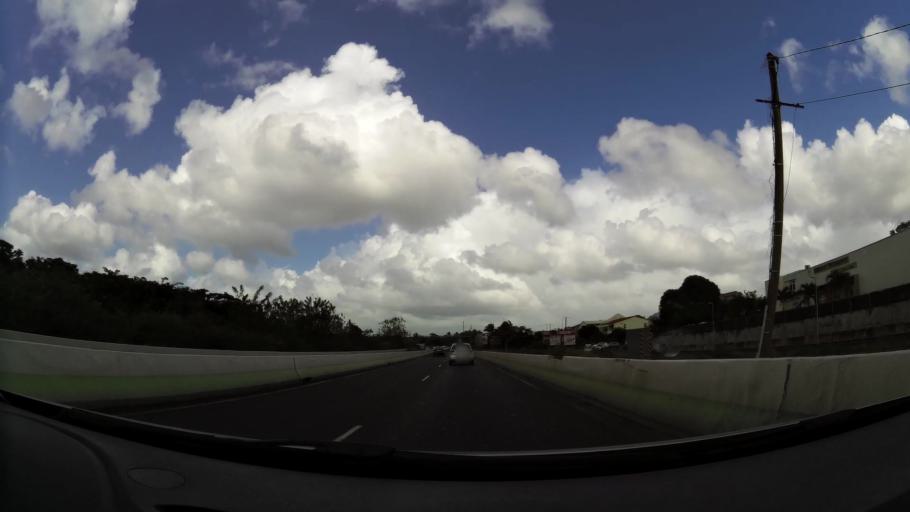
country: MQ
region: Martinique
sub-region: Martinique
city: Ducos
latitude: 14.5288
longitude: -60.9827
